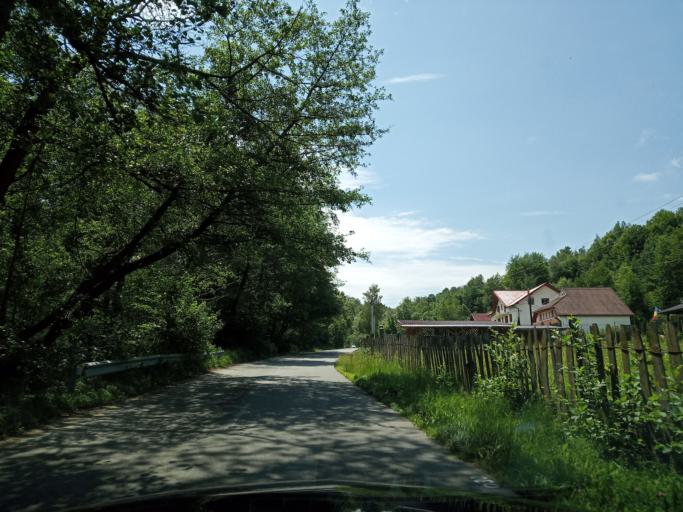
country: RO
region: Hunedoara
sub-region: Oras Petrila
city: Petrila
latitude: 45.4095
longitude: 23.4118
